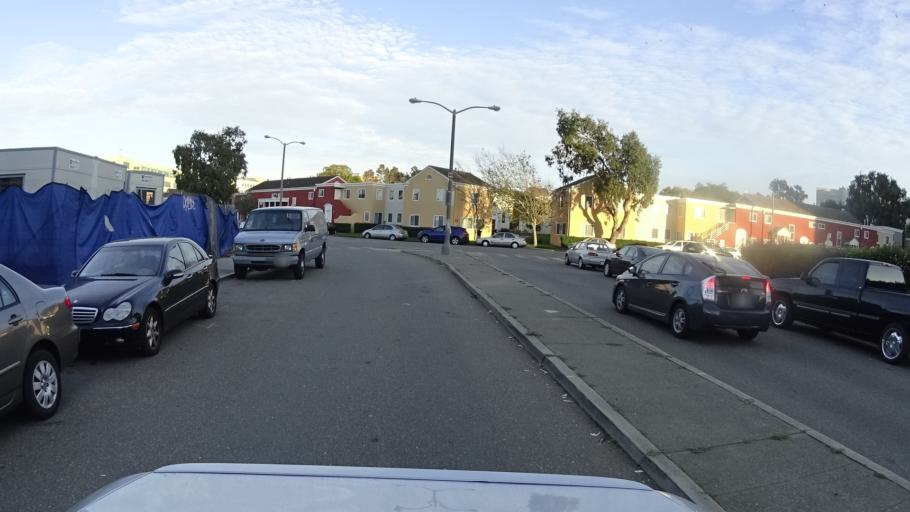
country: US
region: California
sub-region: San Mateo County
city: Daly City
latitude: 37.7212
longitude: -122.4834
